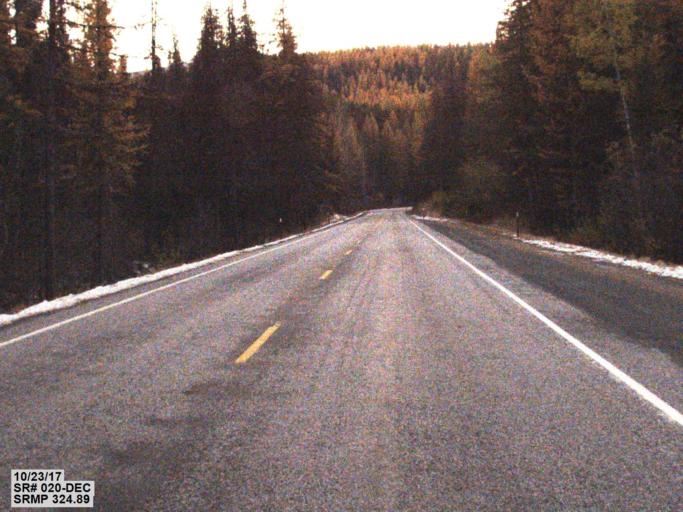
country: US
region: Washington
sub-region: Ferry County
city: Republic
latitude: 48.6231
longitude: -118.4249
